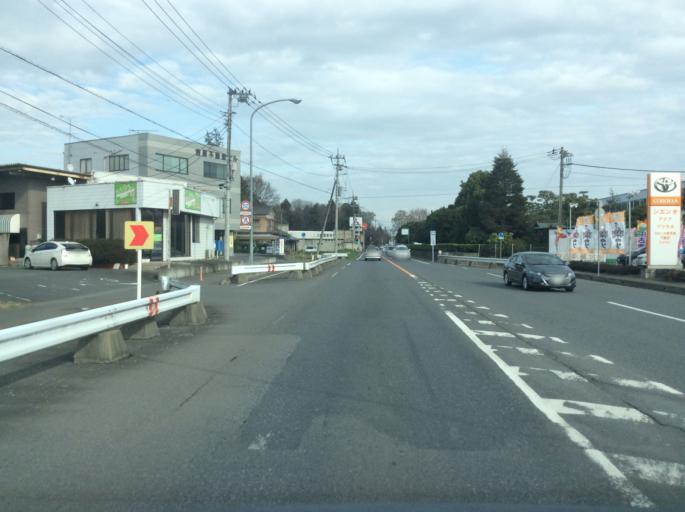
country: JP
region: Ibaraki
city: Tsukuba
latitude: 36.1892
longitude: 140.0210
